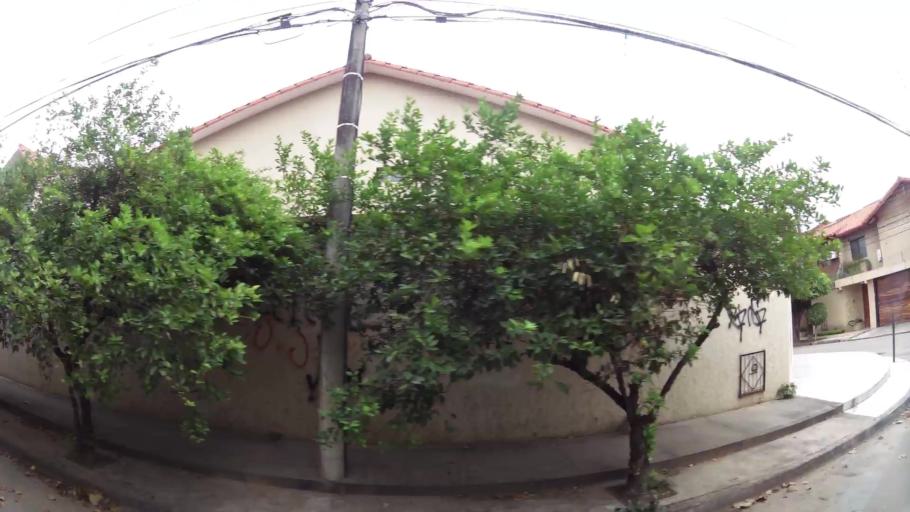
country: BO
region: Santa Cruz
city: Santa Cruz de la Sierra
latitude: -17.7631
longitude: -63.1695
